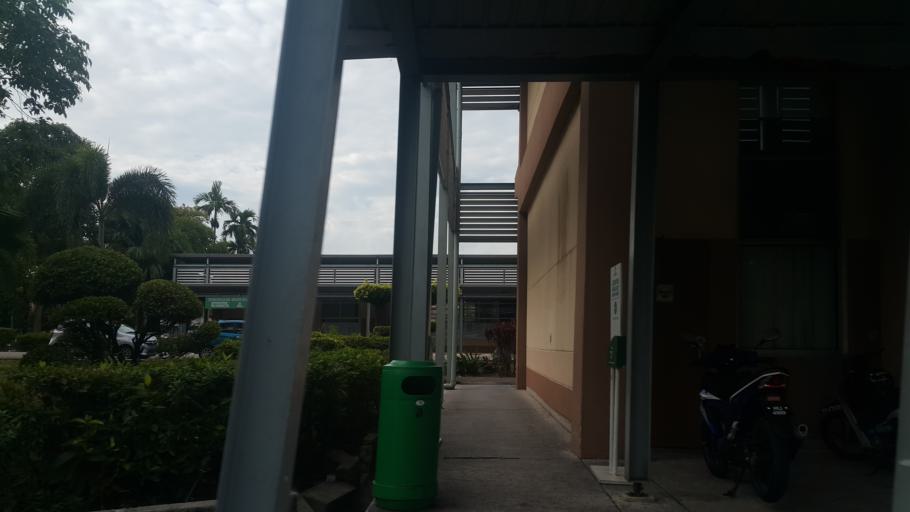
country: MY
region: Johor
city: Pekan Nenas
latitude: 1.3760
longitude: 103.5989
